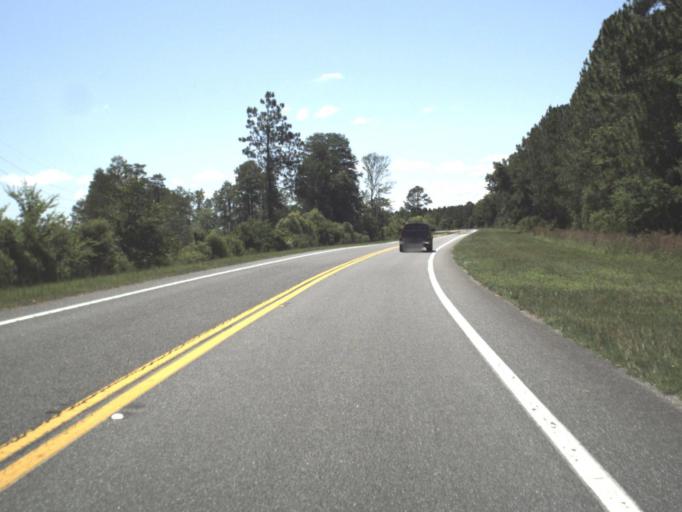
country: US
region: Florida
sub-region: Lafayette County
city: Mayo
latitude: 30.1273
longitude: -83.3558
